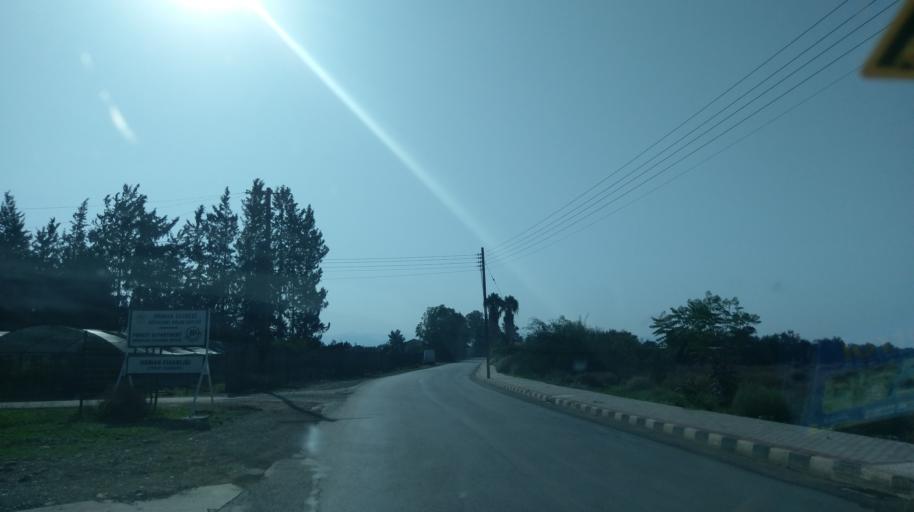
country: CY
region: Lefkosia
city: Morfou
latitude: 35.1942
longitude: 32.9824
